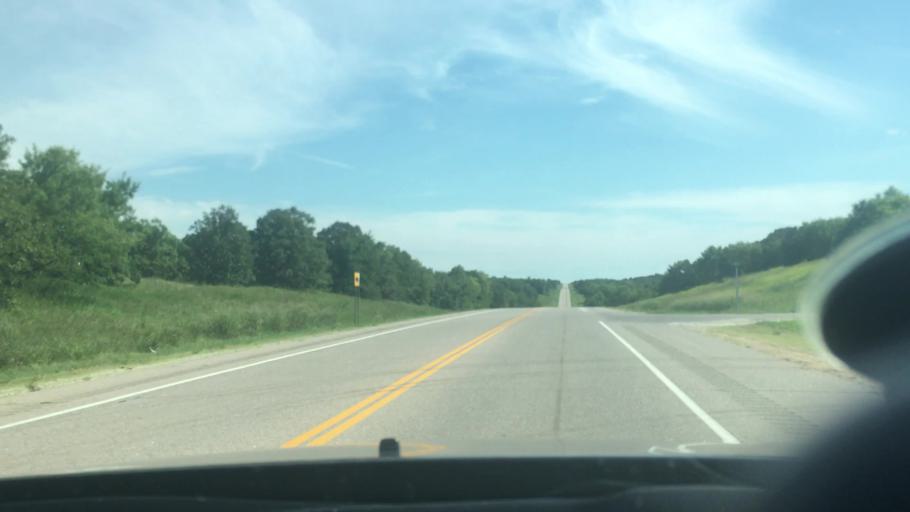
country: US
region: Oklahoma
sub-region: Seminole County
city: Maud
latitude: 35.1164
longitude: -96.6789
